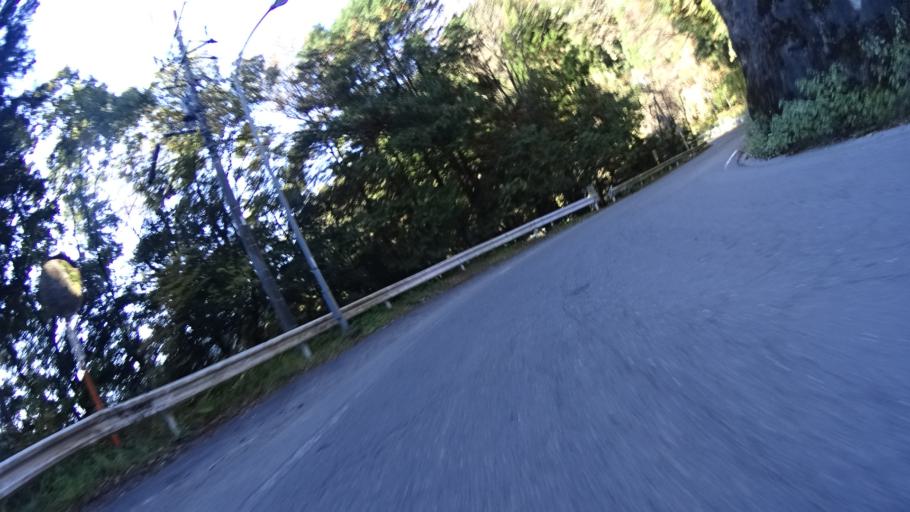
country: JP
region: Yamanashi
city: Uenohara
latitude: 35.6793
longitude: 139.0980
